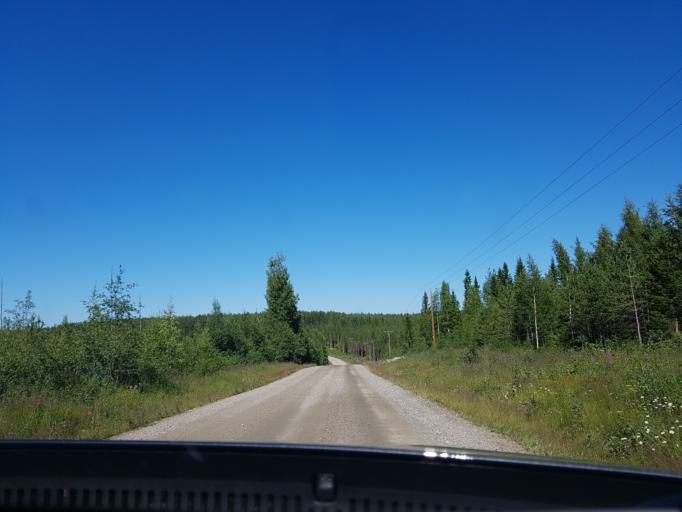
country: FI
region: Kainuu
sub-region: Kehys-Kainuu
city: Kuhmo
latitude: 64.1732
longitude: 29.6367
